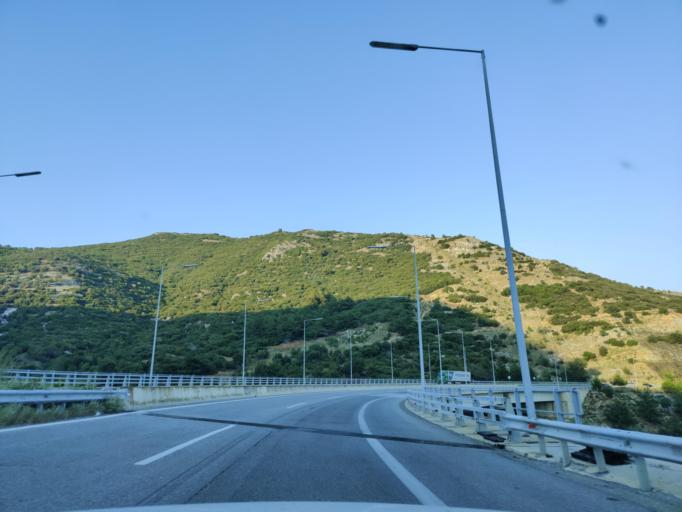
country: GR
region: East Macedonia and Thrace
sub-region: Nomos Kavalas
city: Kavala
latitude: 40.9650
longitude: 24.4303
